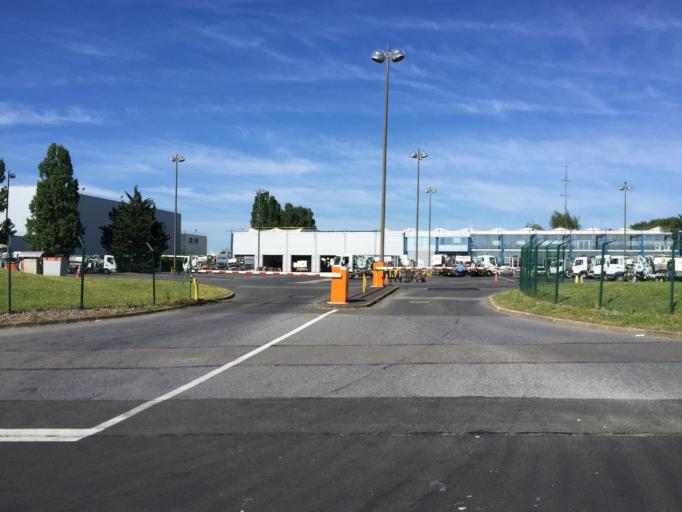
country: FR
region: Ile-de-France
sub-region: Departement du Val-d'Oise
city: Roissy-en-France
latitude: 49.0045
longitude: 2.5524
